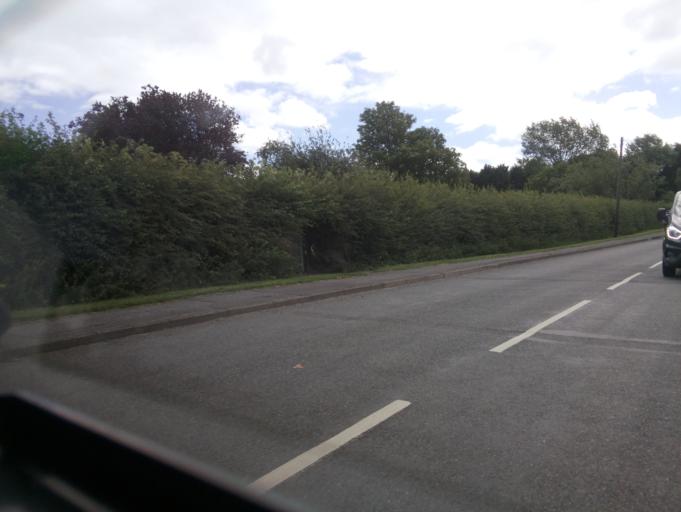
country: GB
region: England
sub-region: Nottinghamshire
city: Cotgrave
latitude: 52.8783
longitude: -1.0797
